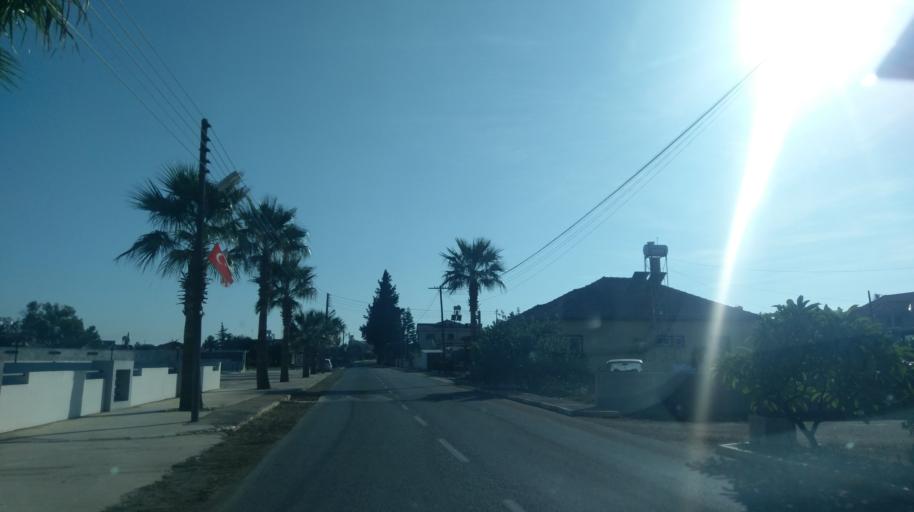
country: CY
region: Larnaka
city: Pergamos
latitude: 35.0485
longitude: 33.7092
